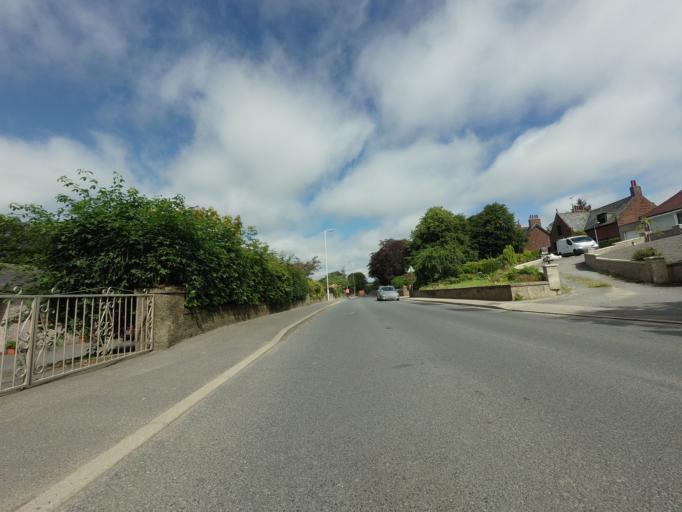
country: GB
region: Scotland
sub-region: Aberdeenshire
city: Turriff
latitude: 57.5394
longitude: -2.4701
